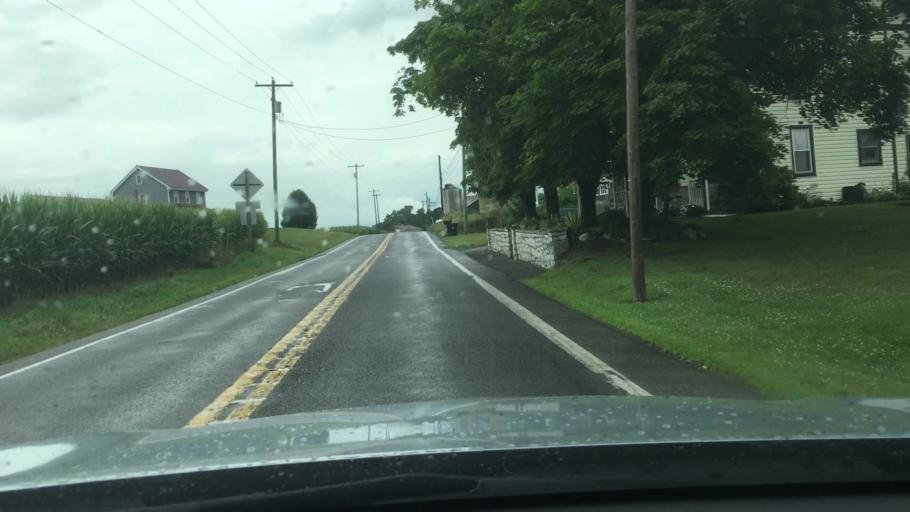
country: US
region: Pennsylvania
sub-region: Franklin County
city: Chambersburg
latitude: 39.8900
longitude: -77.7230
